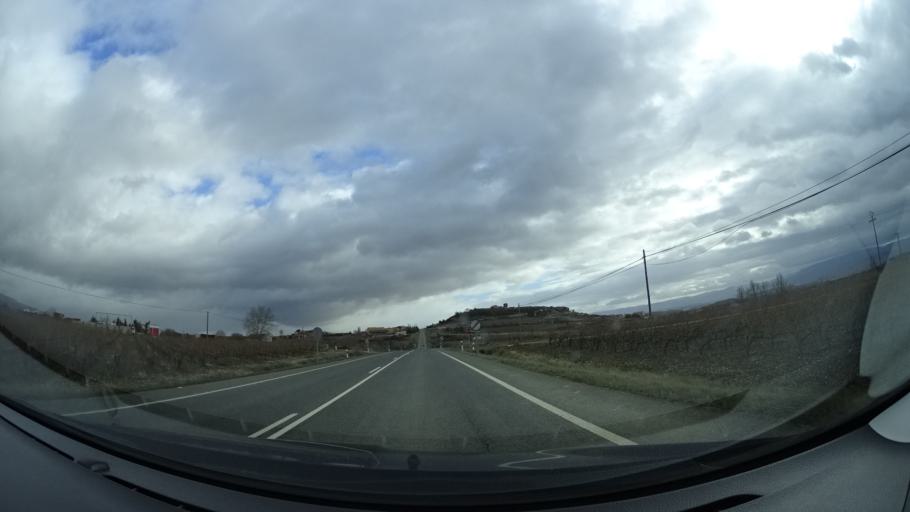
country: ES
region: Basque Country
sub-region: Provincia de Alava
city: Laguardia
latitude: 42.5634
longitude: -2.5985
